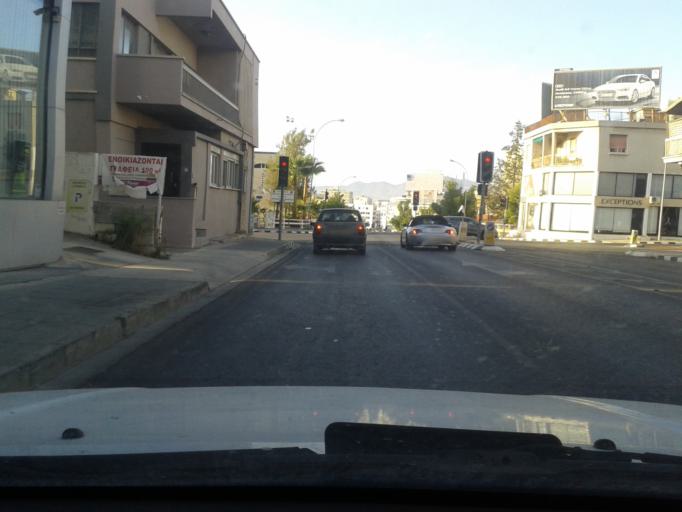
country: CY
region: Lefkosia
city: Nicosia
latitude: 35.1512
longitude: 33.3596
